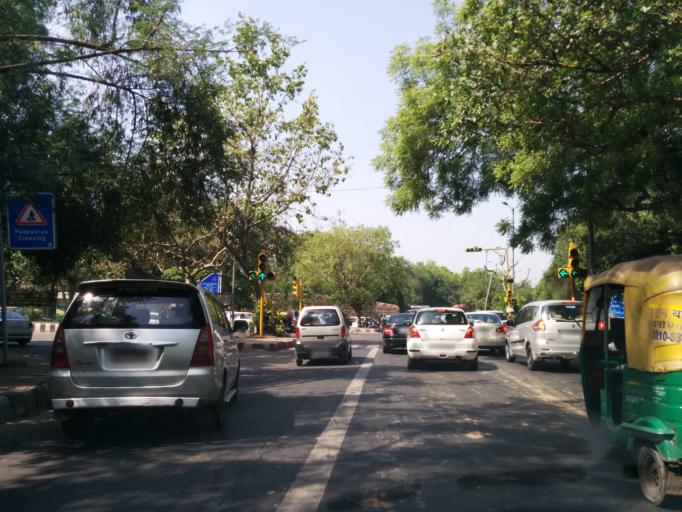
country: IN
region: NCT
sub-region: New Delhi
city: New Delhi
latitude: 28.5321
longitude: 77.1952
